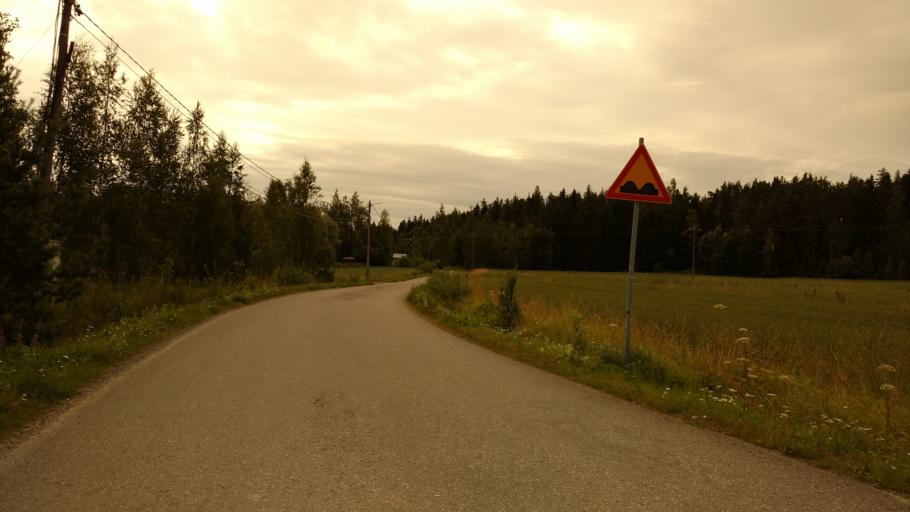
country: FI
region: Varsinais-Suomi
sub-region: Turku
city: Kaarina
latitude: 60.4426
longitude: 22.4327
